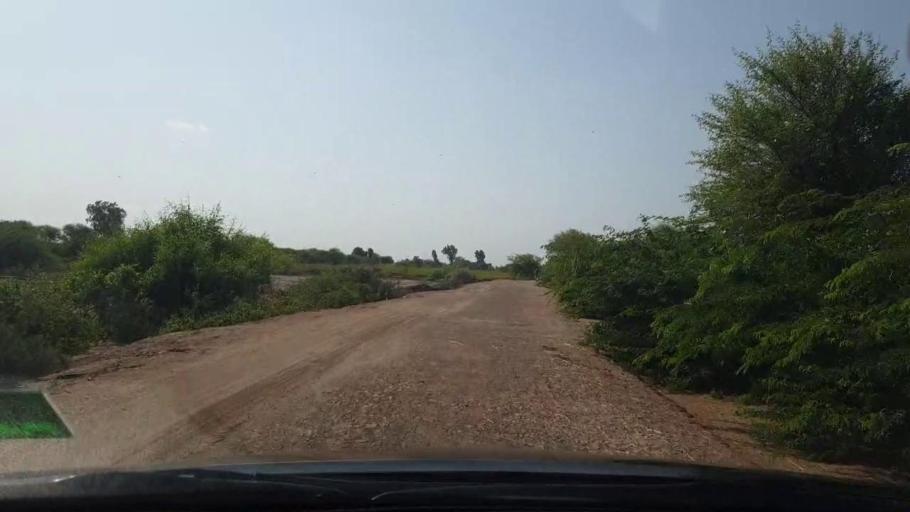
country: PK
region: Sindh
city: Tando Bago
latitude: 24.7502
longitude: 68.9867
